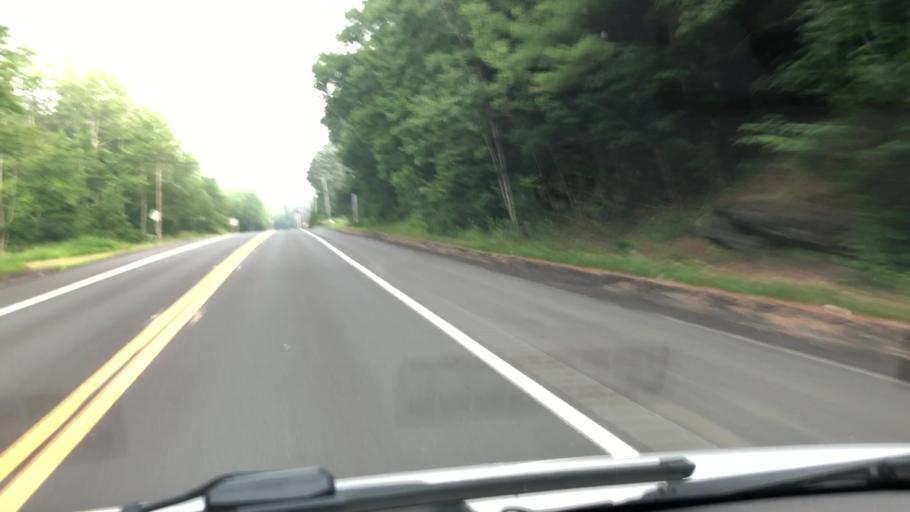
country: US
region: Massachusetts
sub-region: Hampshire County
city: Chesterfield
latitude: 42.4474
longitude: -72.8093
